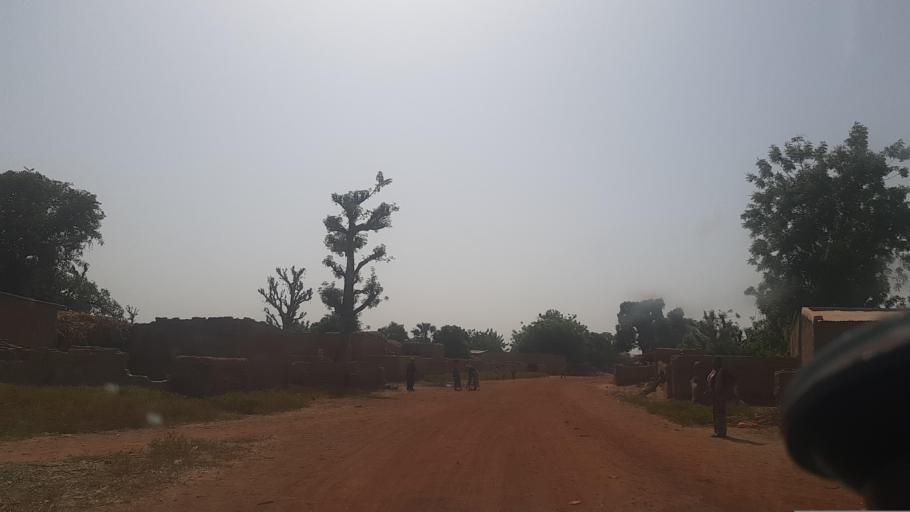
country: ML
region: Segou
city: Baroueli
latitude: 13.0134
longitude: -6.4229
